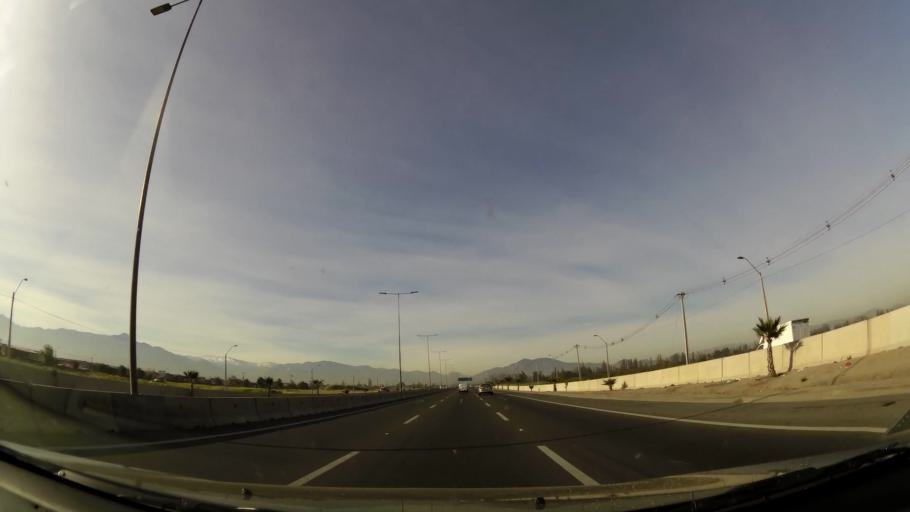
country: CL
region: Santiago Metropolitan
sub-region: Provincia de Santiago
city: La Pintana
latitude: -33.5716
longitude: -70.6126
